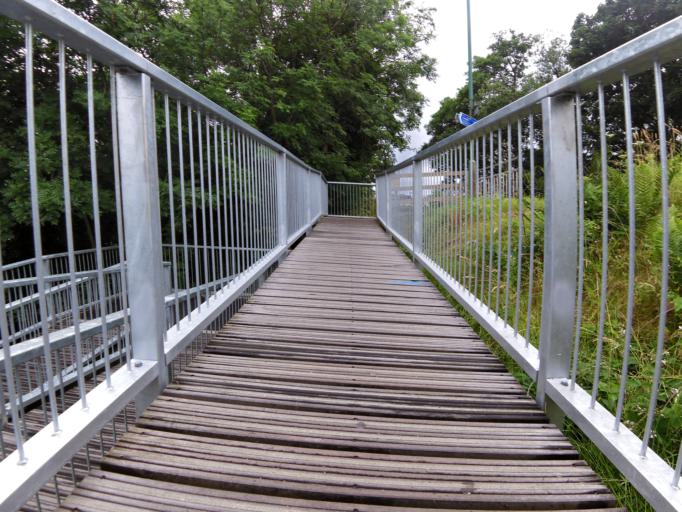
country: GB
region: Scotland
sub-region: Highland
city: Fort William
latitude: 56.8336
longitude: -5.0842
